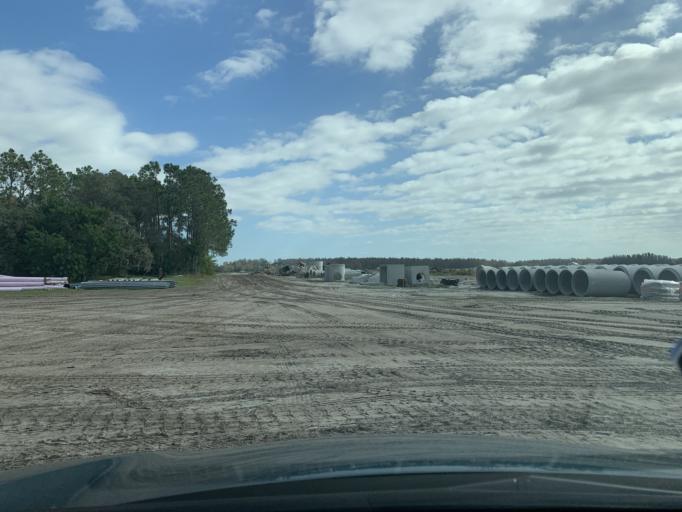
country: US
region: Florida
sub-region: Pasco County
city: Trinity
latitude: 28.2031
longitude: -82.6778
